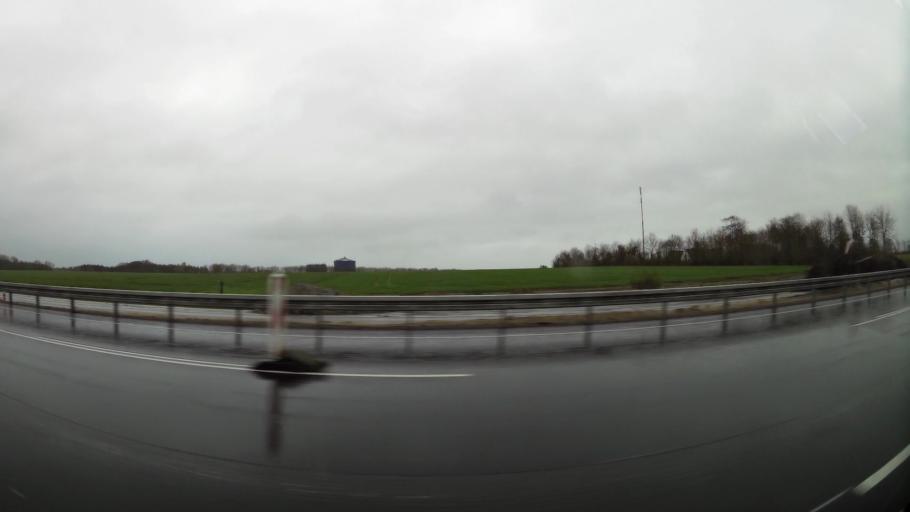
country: DK
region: Central Jutland
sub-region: Herning Kommune
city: Snejbjerg
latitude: 56.2045
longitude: 8.8728
